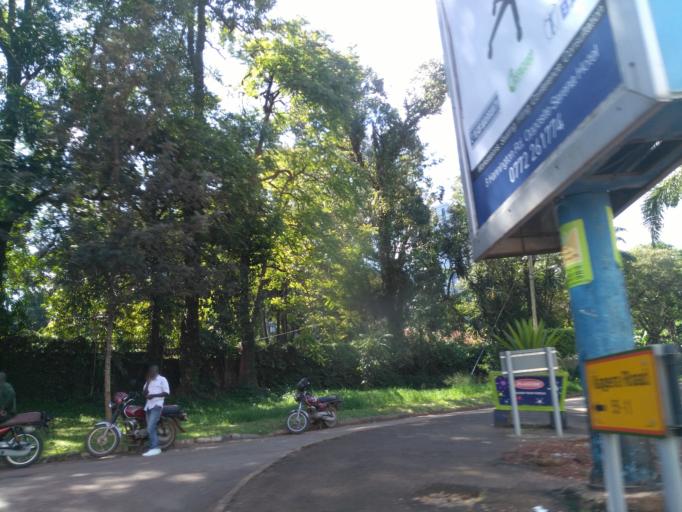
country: UG
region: Central Region
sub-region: Kampala District
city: Kampala
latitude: 0.3210
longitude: 32.5864
